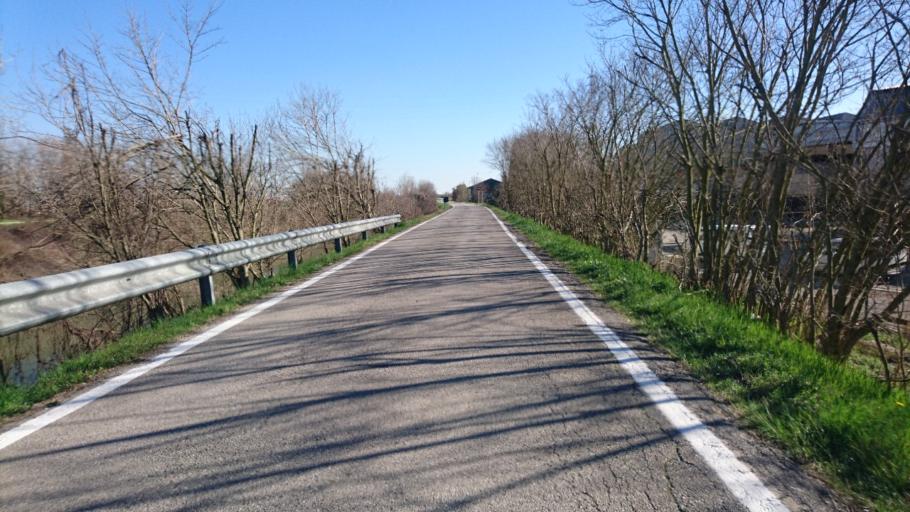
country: IT
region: Veneto
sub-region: Provincia di Padova
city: Battaglia Terme
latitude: 45.2863
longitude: 11.7884
